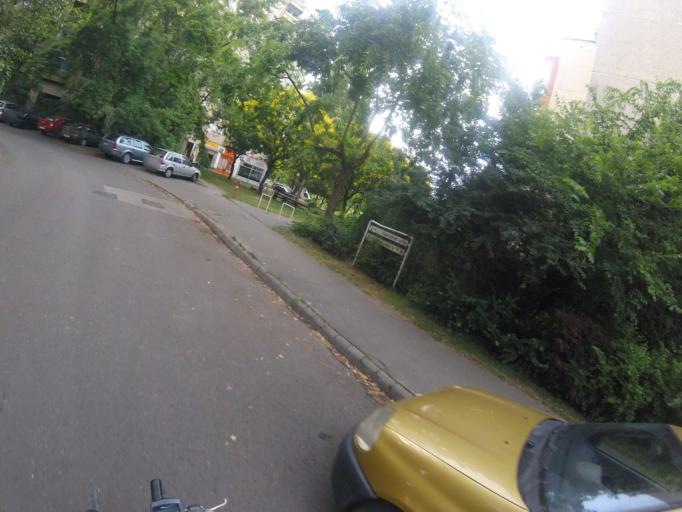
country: HU
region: Budapest
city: Budapest III. keruelet
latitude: 47.5690
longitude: 19.0543
